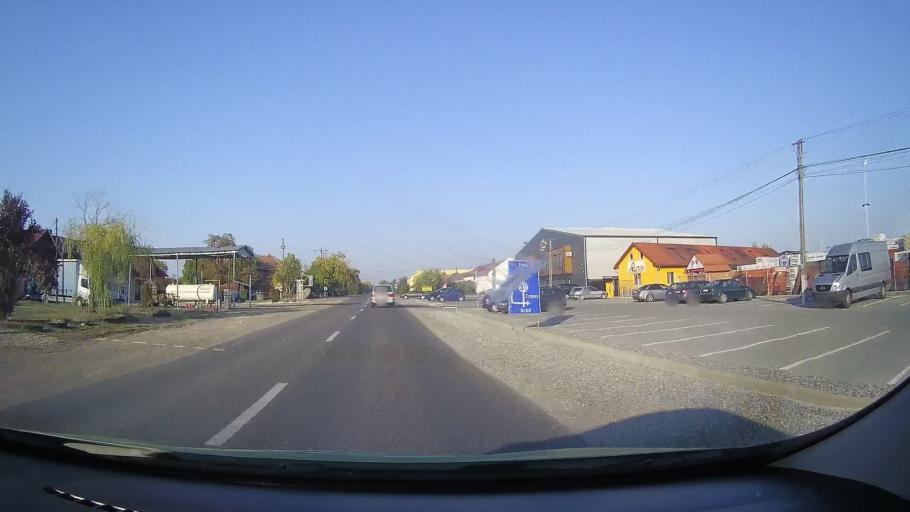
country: RO
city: Masca
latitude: 46.3193
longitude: 21.6843
